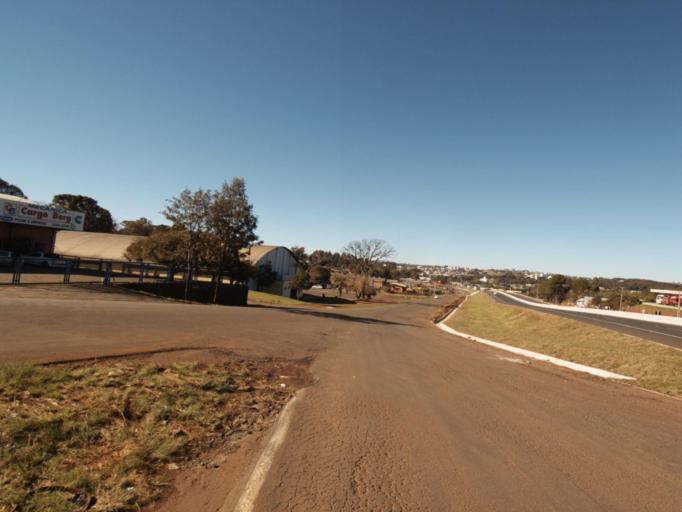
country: BR
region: Santa Catarina
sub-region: Xanxere
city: Xanxere
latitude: -26.8857
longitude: -52.4182
